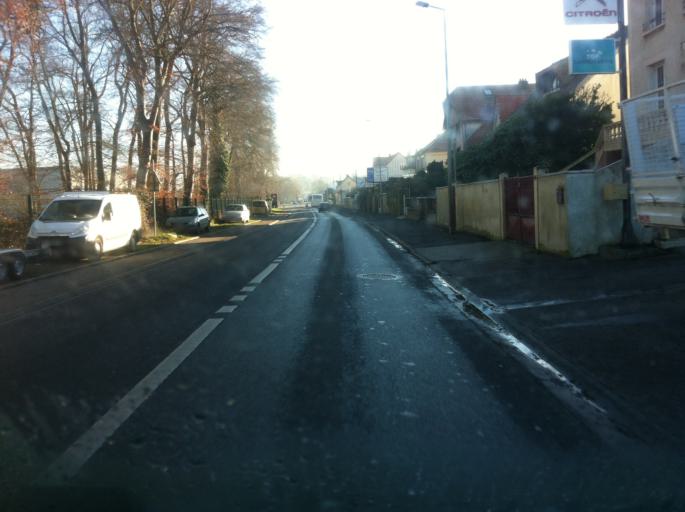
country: FR
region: Picardie
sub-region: Departement de la Somme
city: Mers-les-Bains
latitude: 50.0551
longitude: 1.3905
